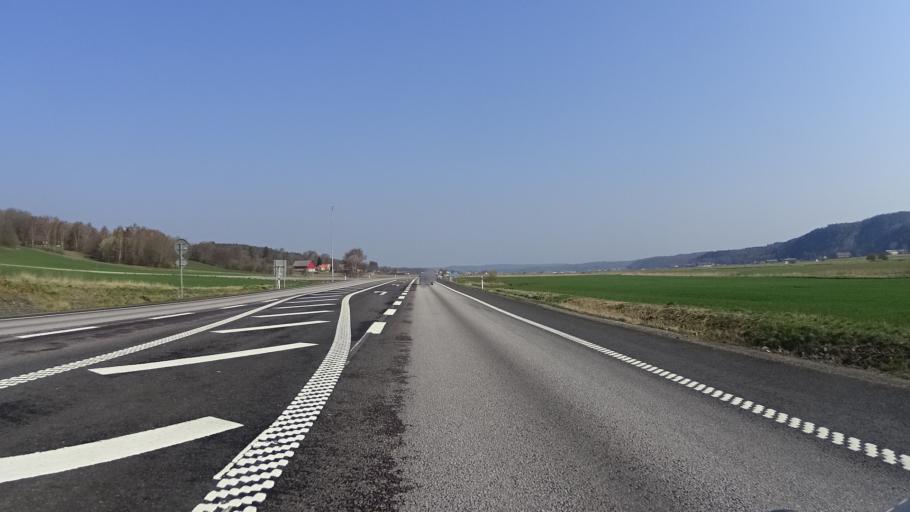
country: SE
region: Halland
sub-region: Varbergs Kommun
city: Veddige
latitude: 57.2092
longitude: 12.3090
